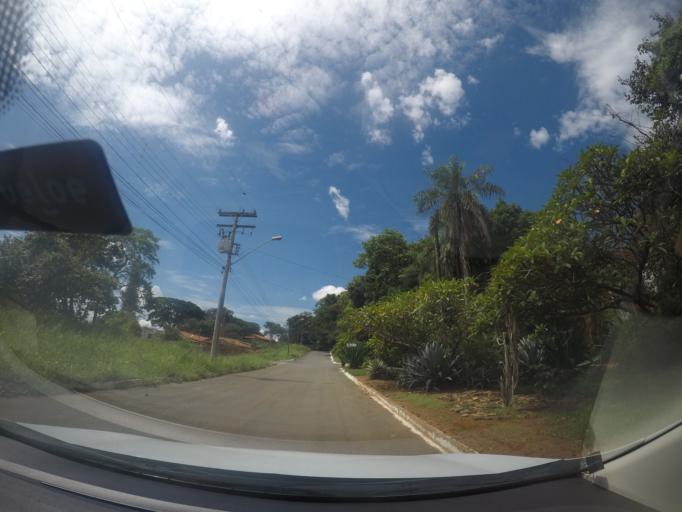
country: BR
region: Goias
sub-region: Goiania
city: Goiania
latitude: -16.6622
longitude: -49.3382
